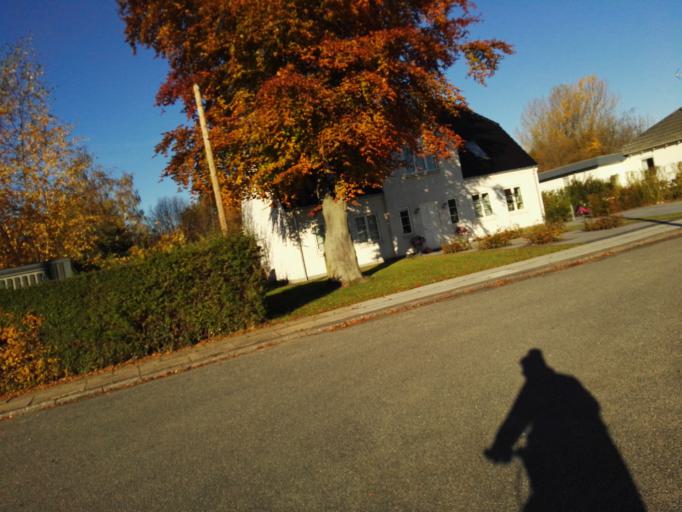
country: DK
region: Capital Region
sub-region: Herlev Kommune
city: Herlev
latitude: 55.7155
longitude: 12.4084
